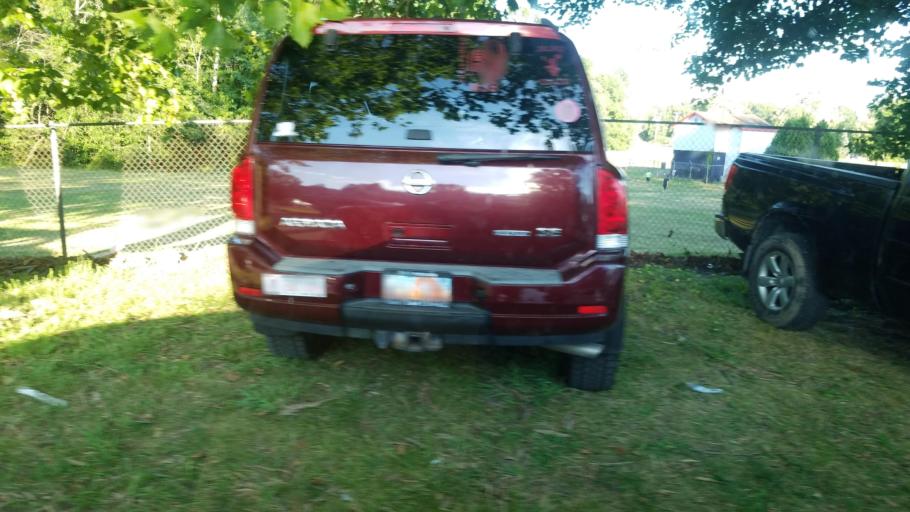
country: US
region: Ohio
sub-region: Trumbull County
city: Niles
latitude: 41.1825
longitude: -80.7857
